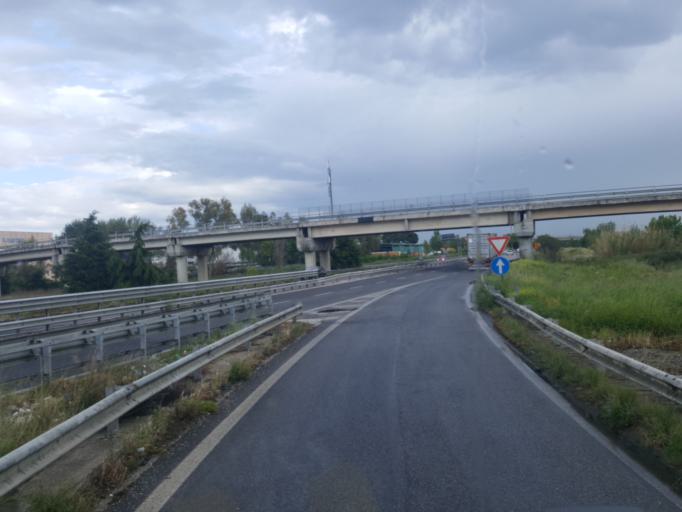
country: IT
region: Campania
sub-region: Provincia di Napoli
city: Pascarola
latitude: 40.9927
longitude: 14.2933
